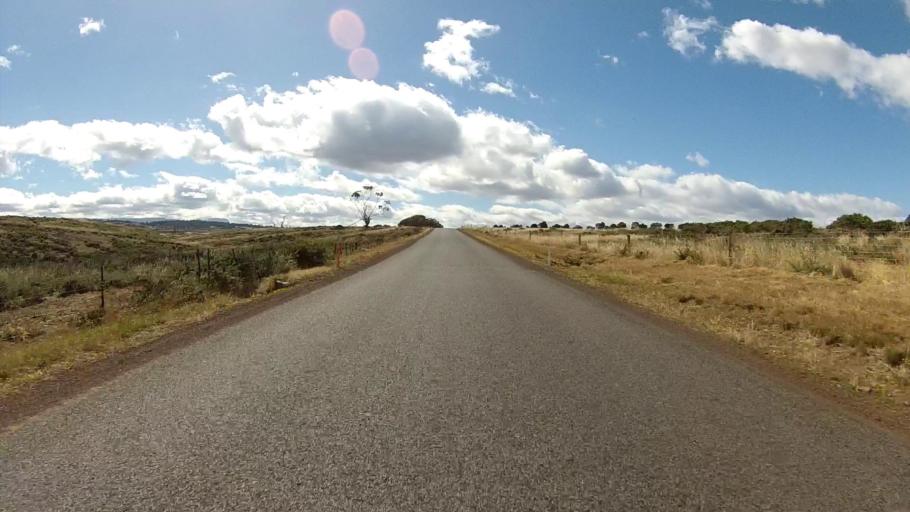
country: AU
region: Tasmania
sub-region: Northern Midlands
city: Evandale
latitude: -41.7071
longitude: 147.3985
